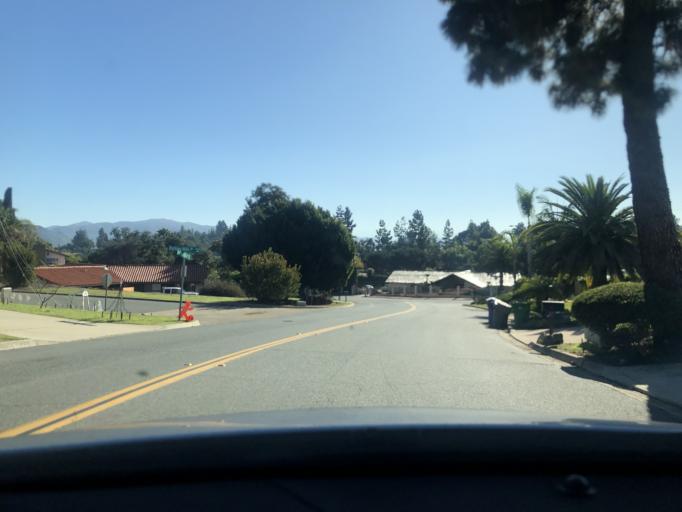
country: US
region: California
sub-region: San Diego County
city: Rancho San Diego
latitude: 32.7698
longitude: -116.9415
